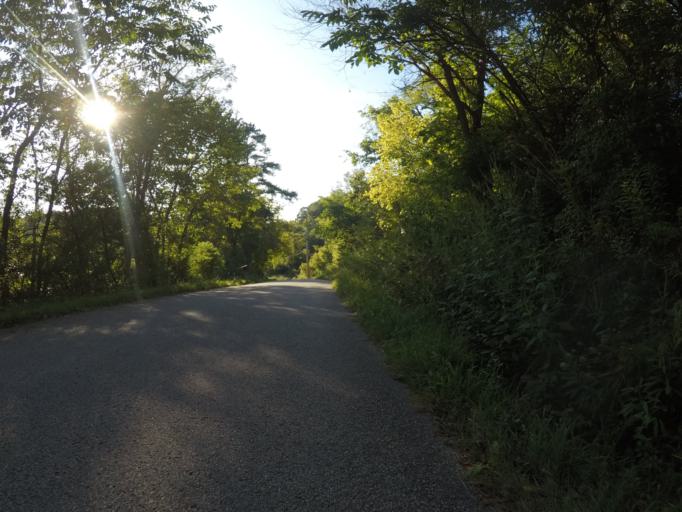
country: US
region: Ohio
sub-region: Lawrence County
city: Burlington
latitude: 38.5234
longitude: -82.5085
